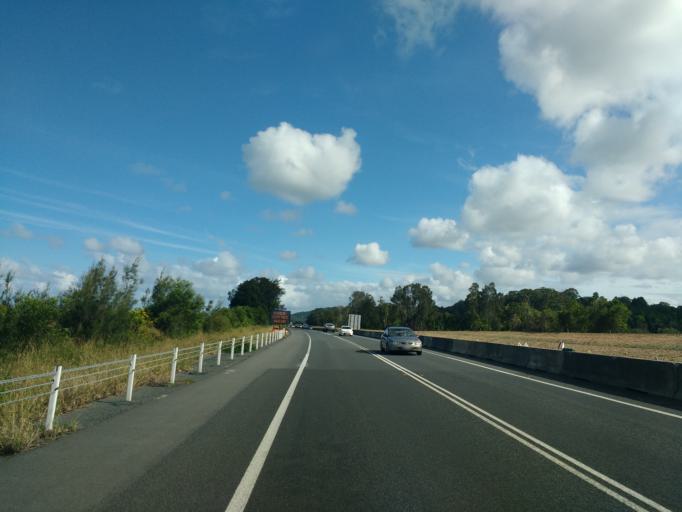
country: AU
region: New South Wales
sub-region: Ballina
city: Ballina
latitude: -28.8703
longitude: 153.4916
